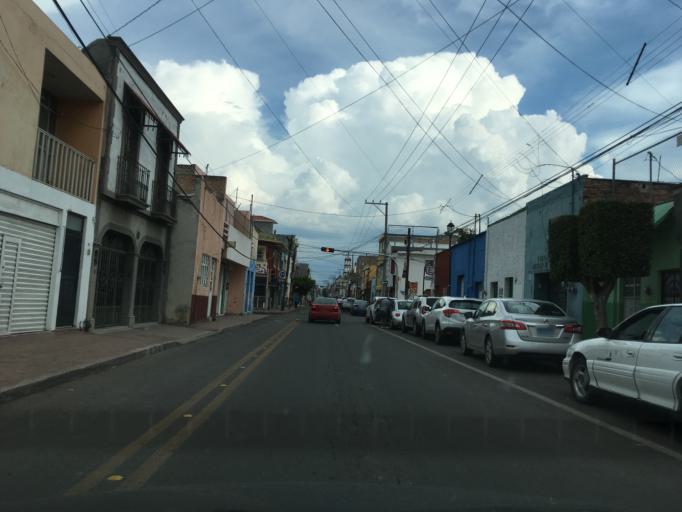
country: MX
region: Guanajuato
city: Celaya
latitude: 20.5277
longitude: -100.8181
